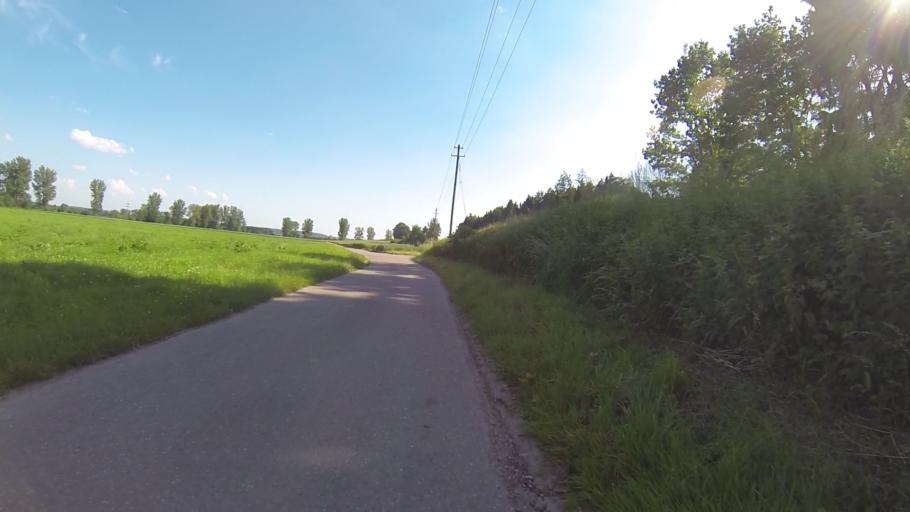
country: DE
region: Baden-Wuerttemberg
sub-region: Tuebingen Region
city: Warthausen
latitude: 48.1844
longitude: 9.8270
